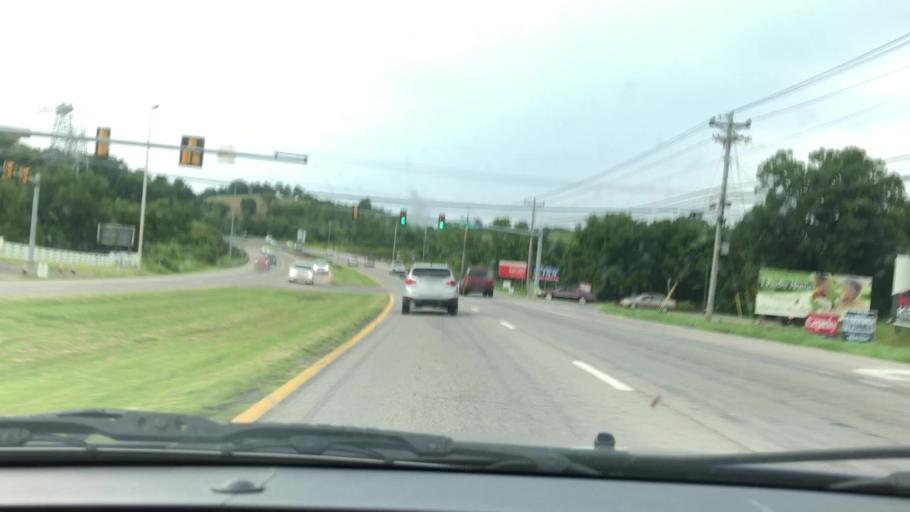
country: US
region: Tennessee
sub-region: Maury County
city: Columbia
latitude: 35.6711
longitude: -87.0039
